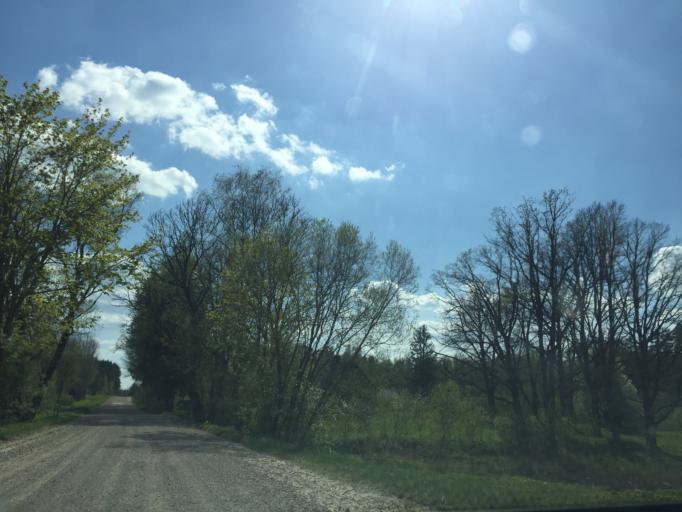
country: LV
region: Vecumnieki
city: Vecumnieki
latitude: 56.4857
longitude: 24.5372
